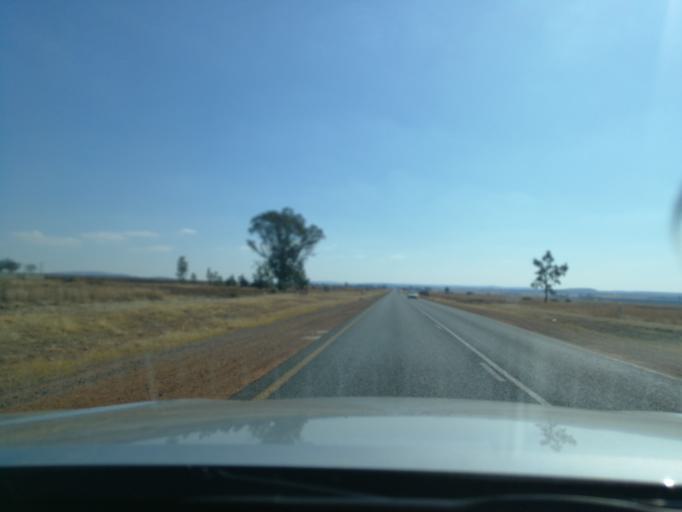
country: ZA
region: North-West
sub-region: Dr Kenneth Kaunda District Municipality
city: Klerksdorp
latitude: -26.8597
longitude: 26.5874
